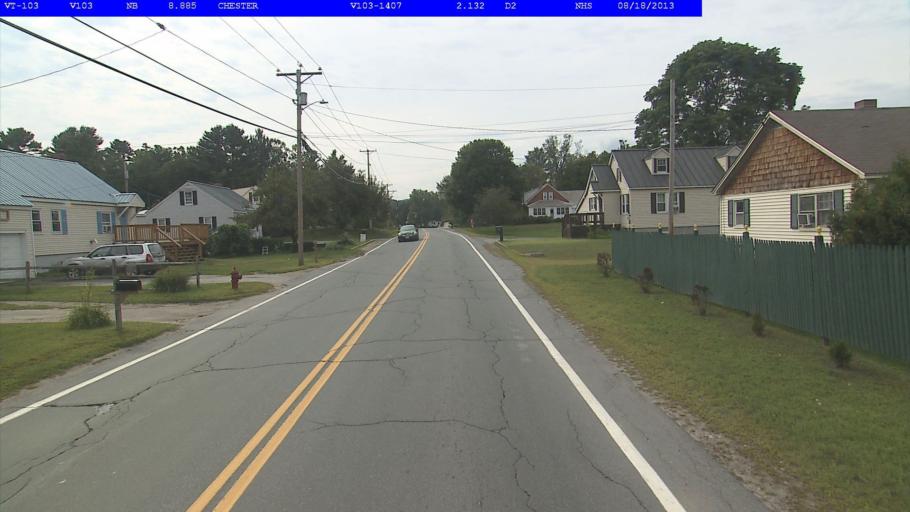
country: US
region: Vermont
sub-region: Windsor County
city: Chester
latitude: 43.2565
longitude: -72.5818
